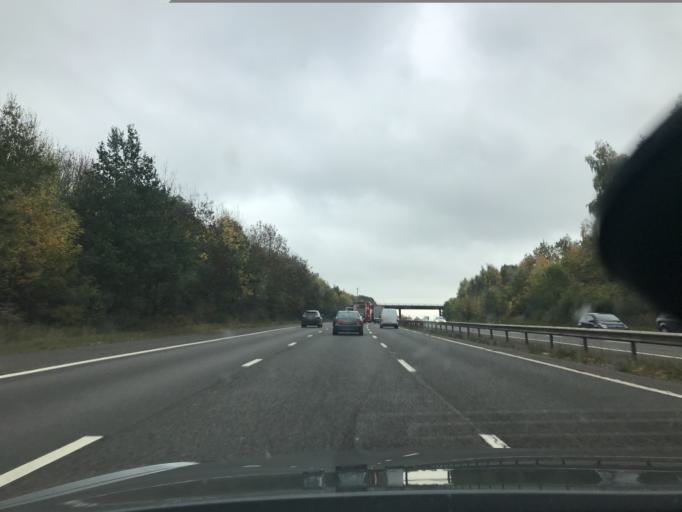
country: GB
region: England
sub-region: Warwickshire
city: Wroxall
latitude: 52.2876
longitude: -1.6671
